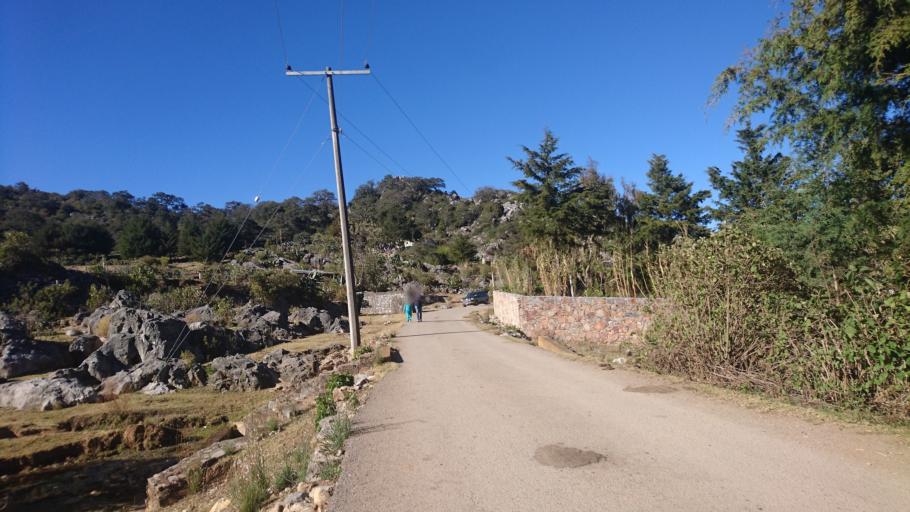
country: MX
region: San Luis Potosi
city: Zaragoza
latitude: 22.0206
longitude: -100.6020
